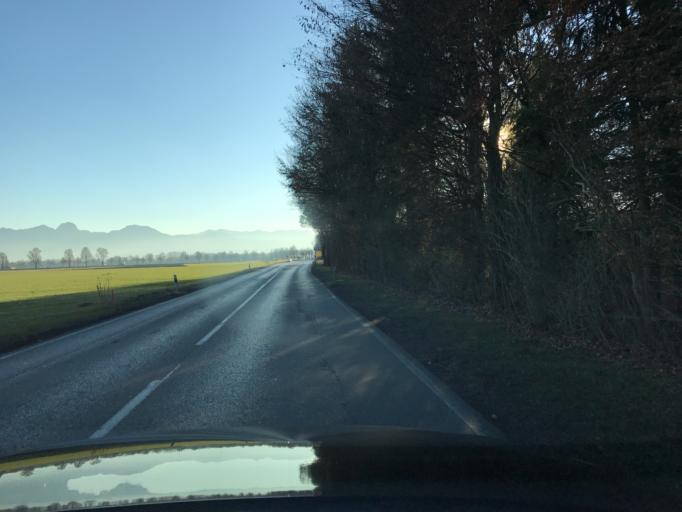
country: DE
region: Bavaria
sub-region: Upper Bavaria
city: Bad Aibling
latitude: 47.8749
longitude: 11.9906
